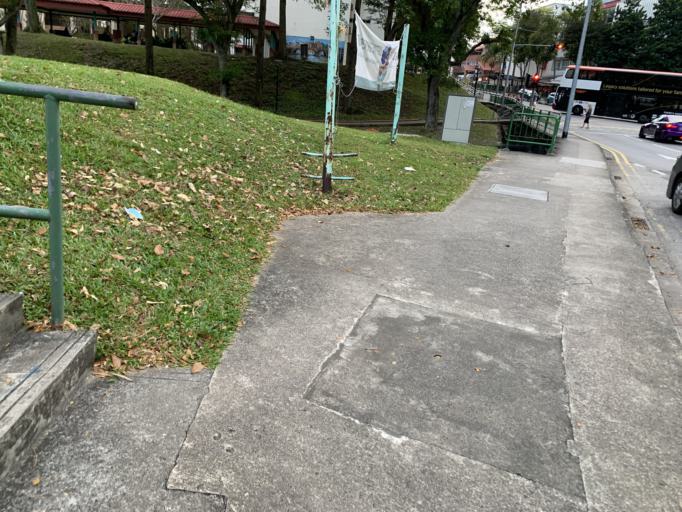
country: SG
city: Singapore
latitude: 1.3101
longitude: 103.7930
